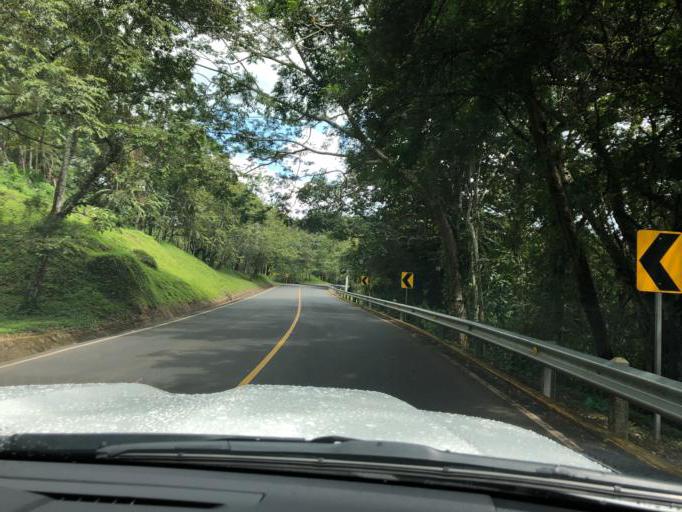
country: NI
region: Chontales
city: Villa Sandino
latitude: 11.9946
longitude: -84.9118
